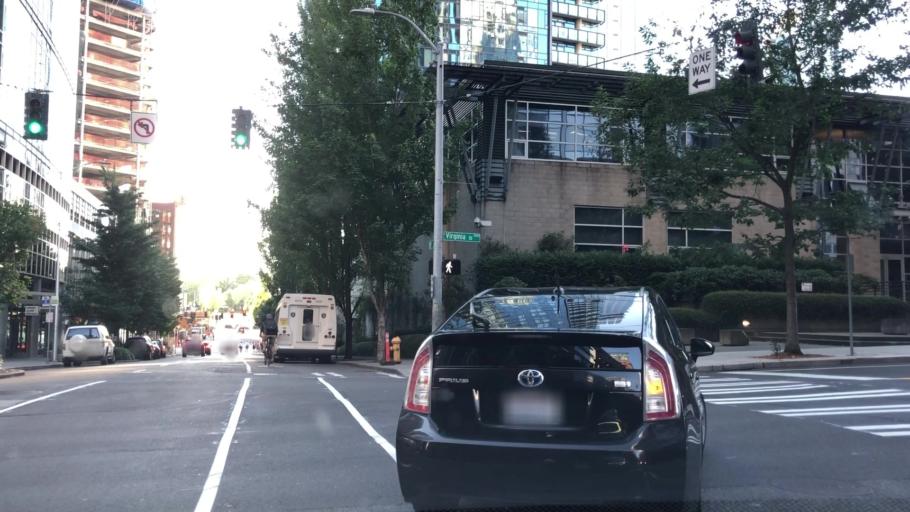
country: US
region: Washington
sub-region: King County
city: Seattle
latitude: 47.6156
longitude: -122.3365
